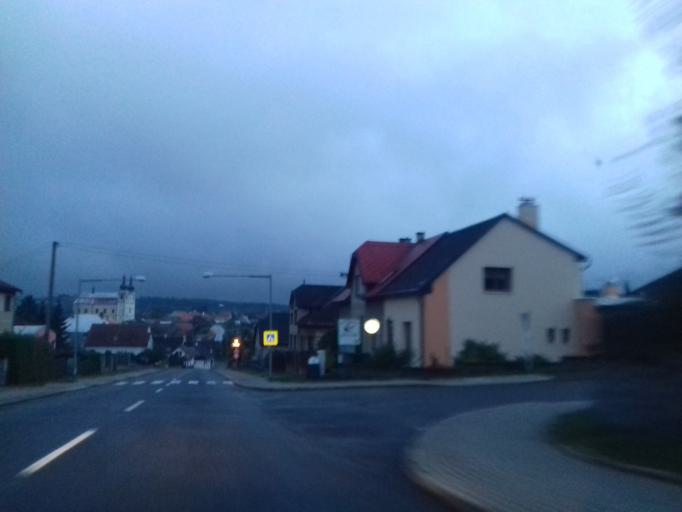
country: CZ
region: Pardubicky
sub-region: Okres Svitavy
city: Bystre
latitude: 49.6330
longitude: 16.3413
